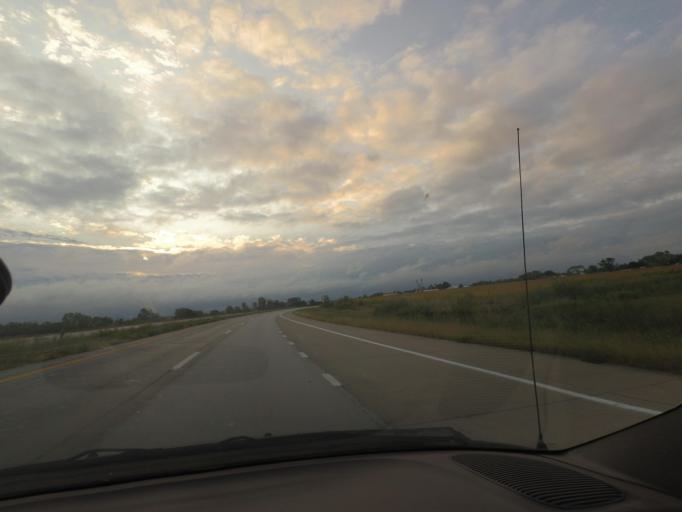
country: US
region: Missouri
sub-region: Shelby County
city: Shelbina
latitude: 39.6975
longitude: -92.0320
